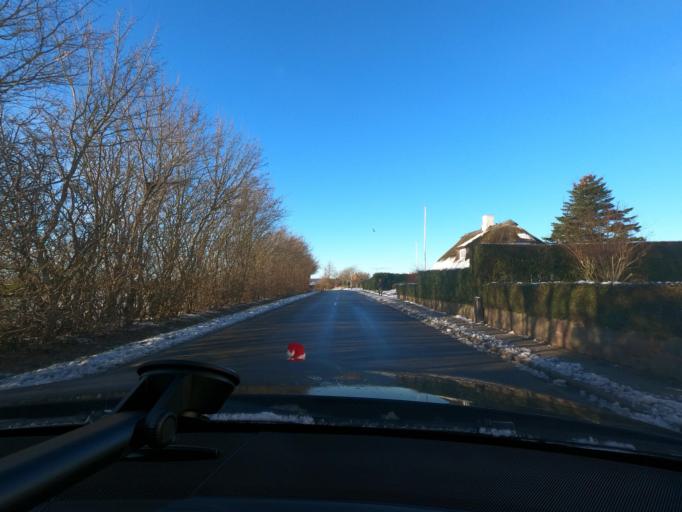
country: DK
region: South Denmark
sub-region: Sonderborg Kommune
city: Horuphav
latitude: 54.8756
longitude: 9.9253
